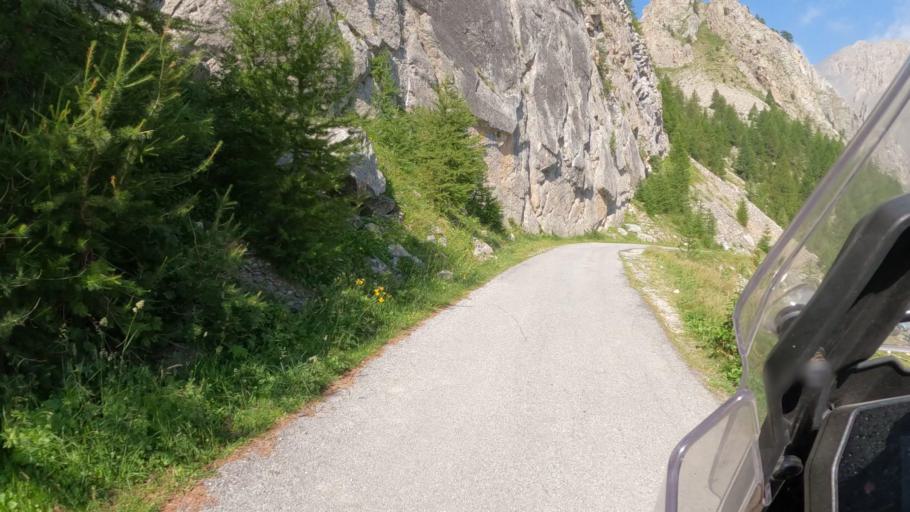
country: IT
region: Piedmont
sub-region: Provincia di Cuneo
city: Pietraporzio
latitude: 44.4051
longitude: 7.0402
